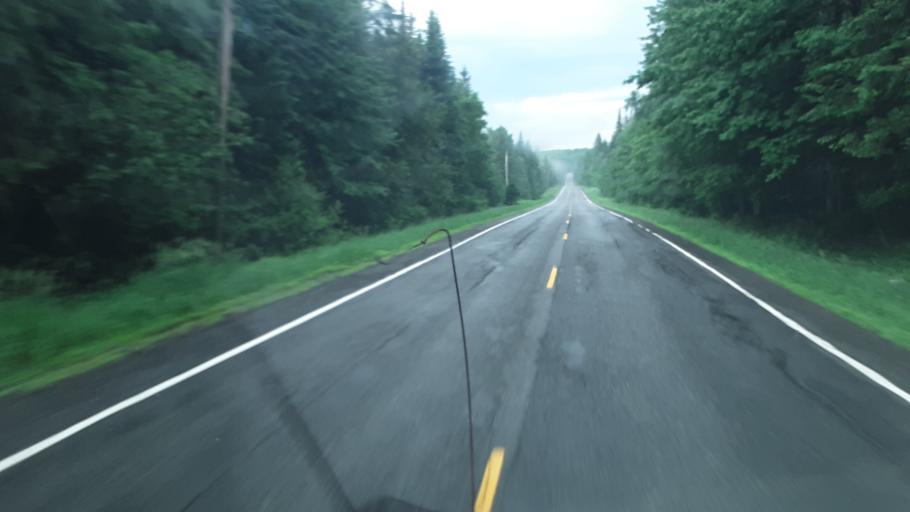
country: US
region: Maine
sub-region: Penobscot County
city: Patten
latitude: 46.1949
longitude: -68.3336
